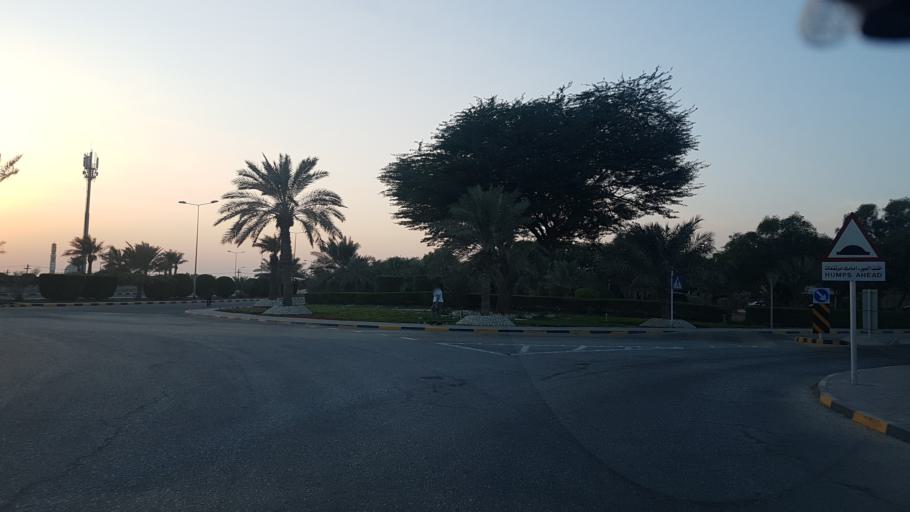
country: BH
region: Northern
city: Ar Rifa'
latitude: 26.0874
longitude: 50.5494
